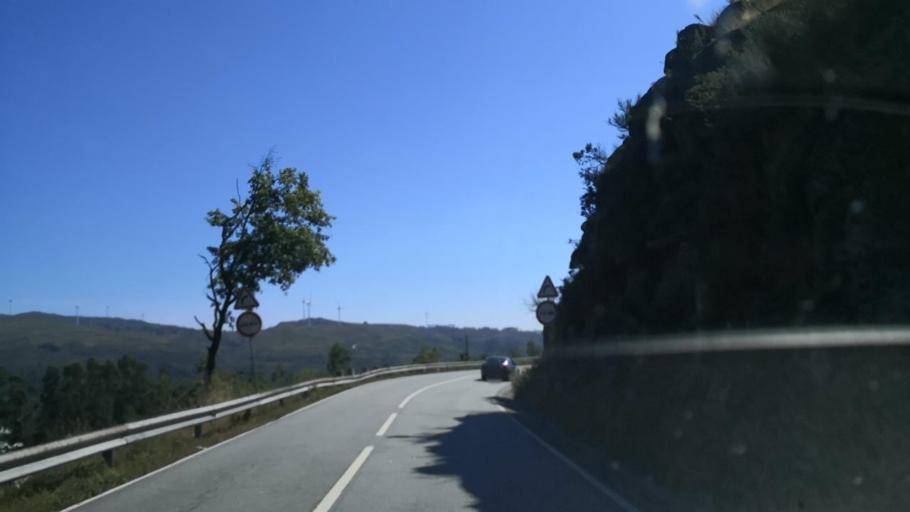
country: PT
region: Braga
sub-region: Fafe
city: Fafe
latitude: 41.4959
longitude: -8.0882
